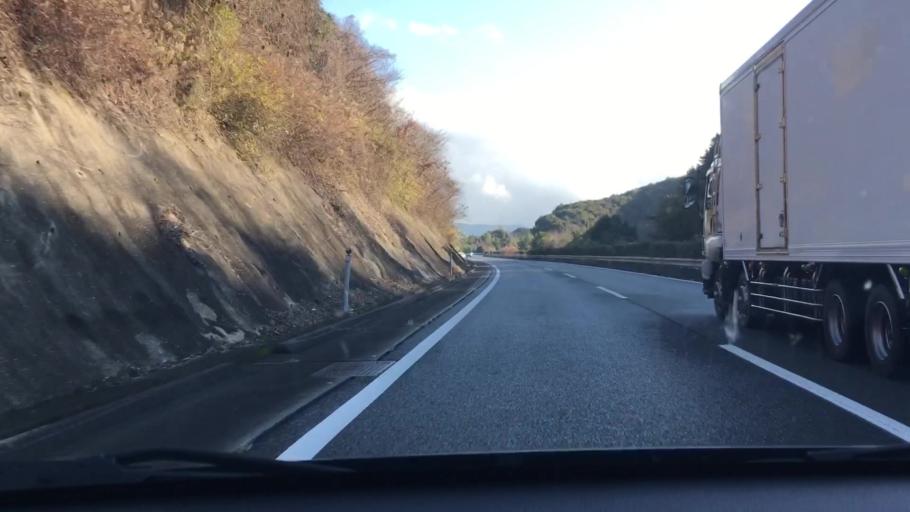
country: JP
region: Kumamoto
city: Hitoyoshi
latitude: 32.1721
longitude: 130.7908
